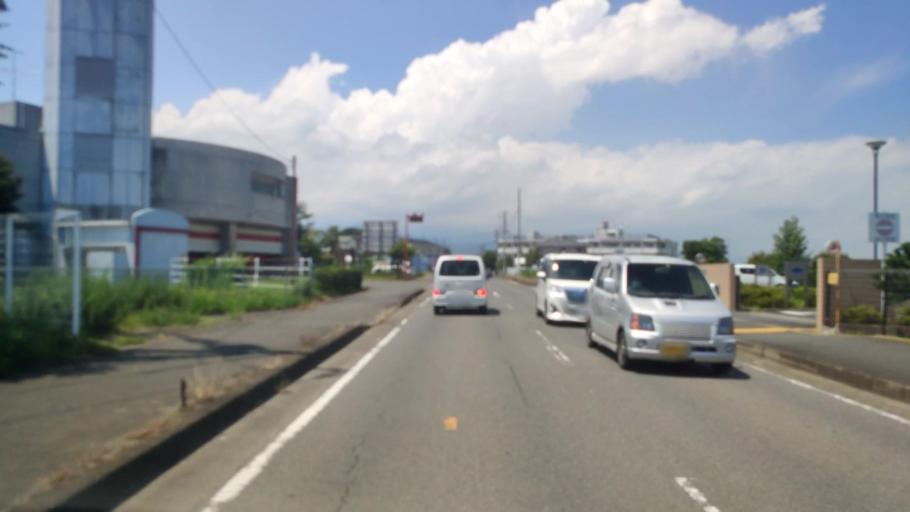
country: JP
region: Kanagawa
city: Oiso
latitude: 35.3449
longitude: 139.3056
